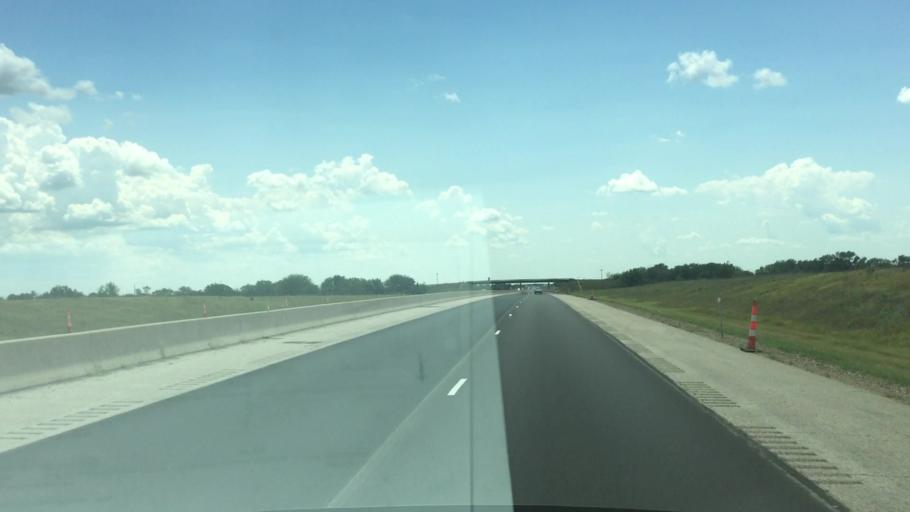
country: US
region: Kansas
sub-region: Lyon County
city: Emporia
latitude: 38.5680
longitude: -96.1024
